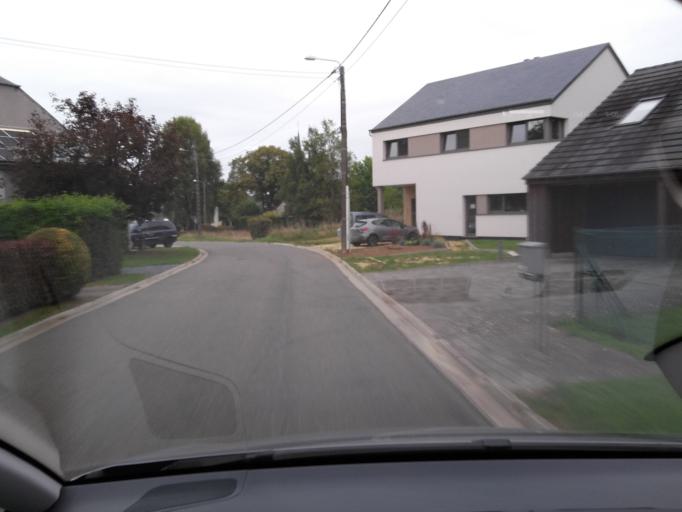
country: BE
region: Wallonia
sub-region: Province du Luxembourg
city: Etalle
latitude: 49.6578
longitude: 5.5709
